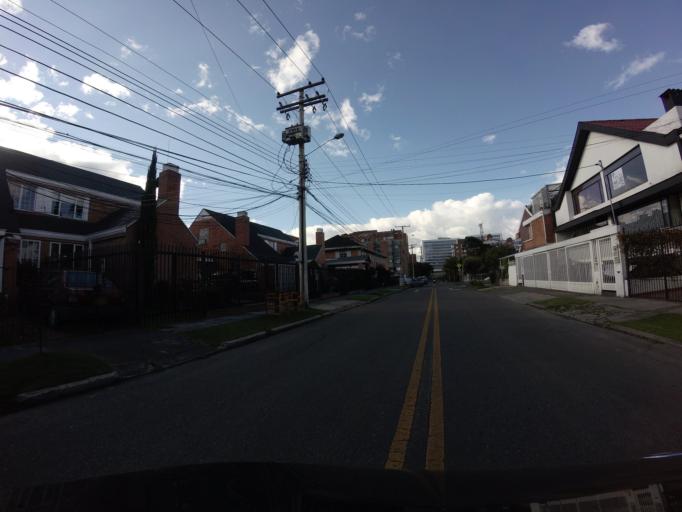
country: CO
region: Bogota D.C.
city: Barrio San Luis
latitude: 4.7058
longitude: -74.0631
